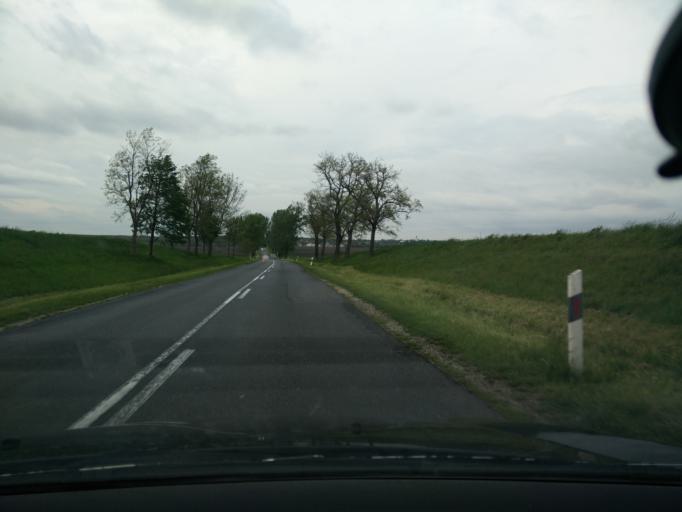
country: HU
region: Gyor-Moson-Sopron
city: Tet
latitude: 47.4440
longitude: 17.4824
